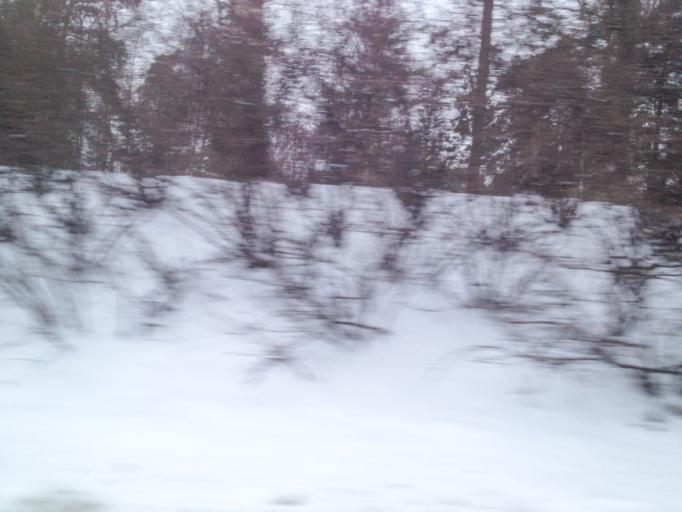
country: FI
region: Uusimaa
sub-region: Helsinki
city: Vantaa
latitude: 60.2076
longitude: 25.1353
